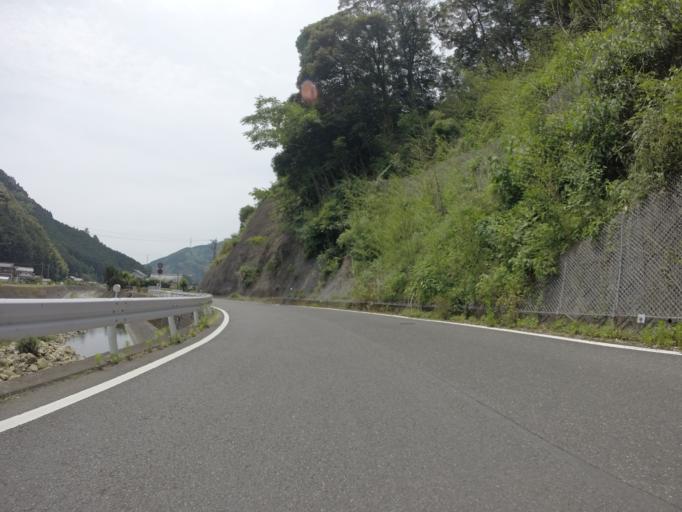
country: JP
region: Shizuoka
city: Shizuoka-shi
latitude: 35.0195
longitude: 138.2828
